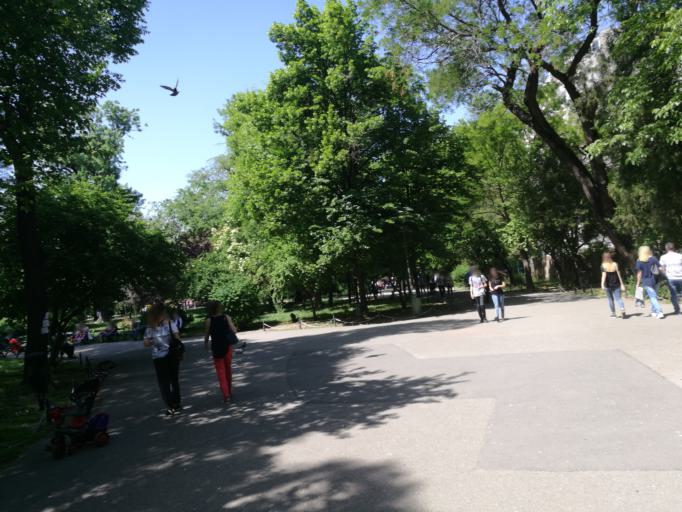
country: RO
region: Bucuresti
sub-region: Municipiul Bucuresti
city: Bucuresti
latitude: 44.4350
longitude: 26.0934
